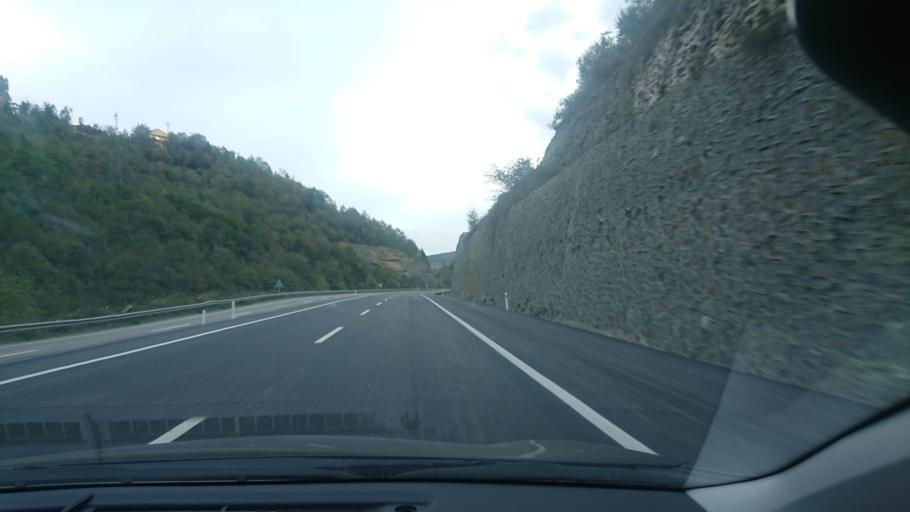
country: TR
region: Zonguldak
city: Beycuma
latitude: 41.3906
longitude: 31.9360
